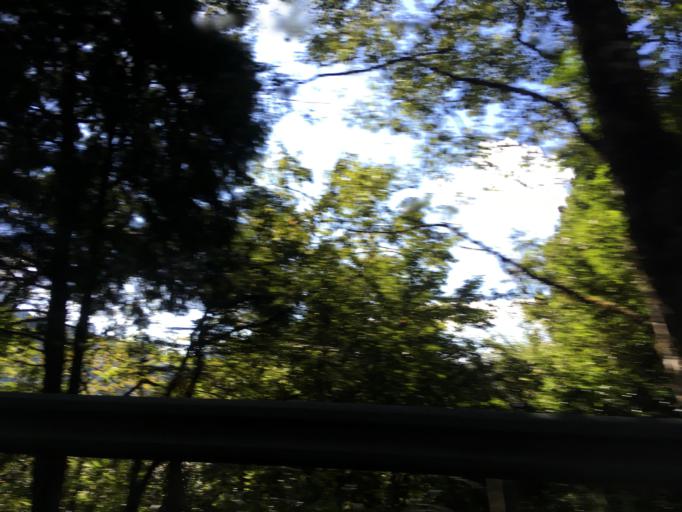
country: TW
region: Taiwan
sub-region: Yilan
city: Yilan
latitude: 24.4992
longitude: 121.5536
